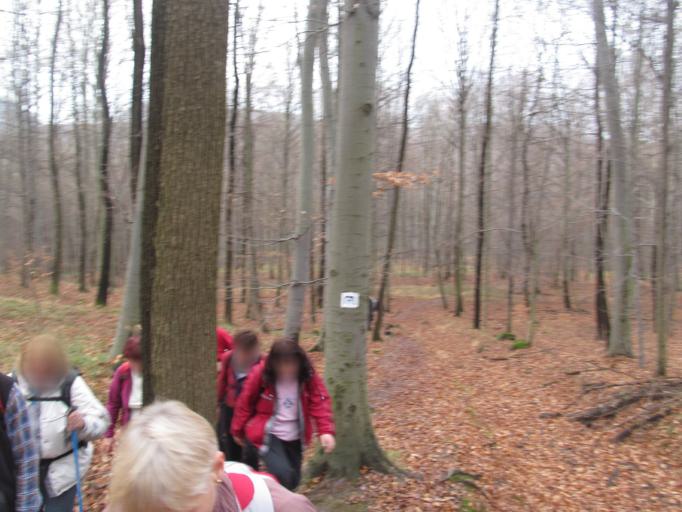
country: HU
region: Komarom-Esztergom
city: Pilismarot
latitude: 47.7352
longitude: 18.8648
